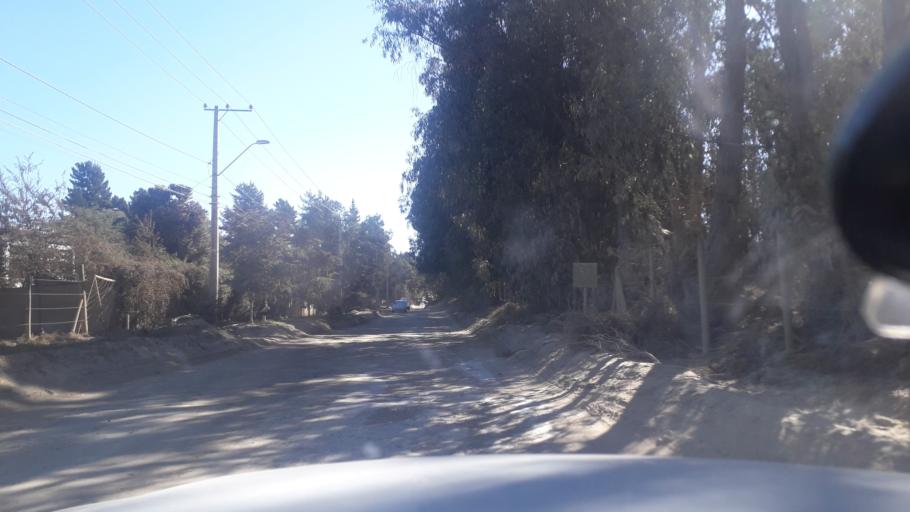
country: CL
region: Valparaiso
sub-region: Provincia de Valparaiso
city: Vina del Mar
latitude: -32.9583
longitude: -71.5148
